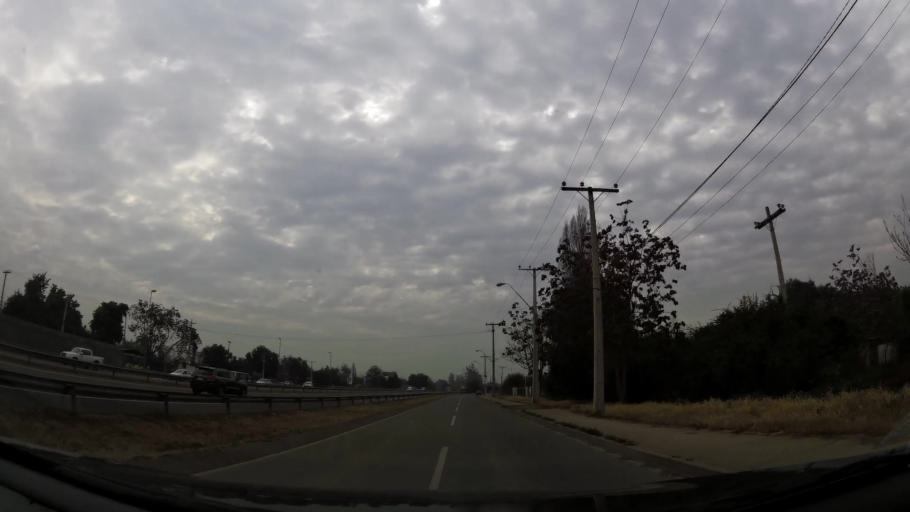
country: CL
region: Santiago Metropolitan
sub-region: Provincia de Chacabuco
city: Chicureo Abajo
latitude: -33.2353
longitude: -70.6943
